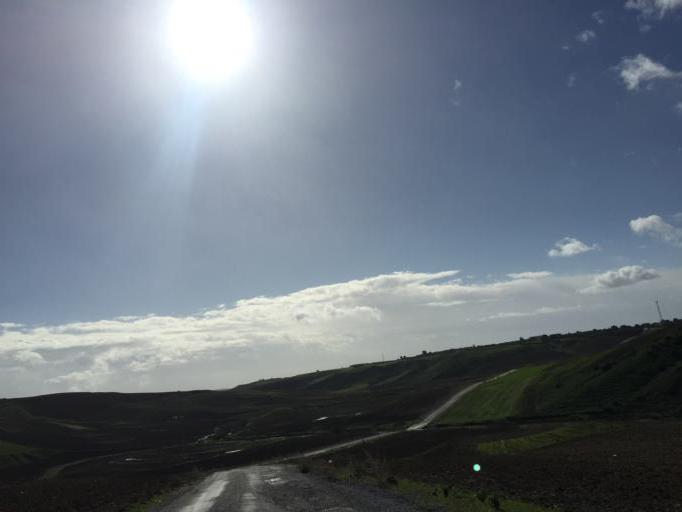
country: TN
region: Nabul
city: El Mida
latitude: 36.8615
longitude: 10.8605
